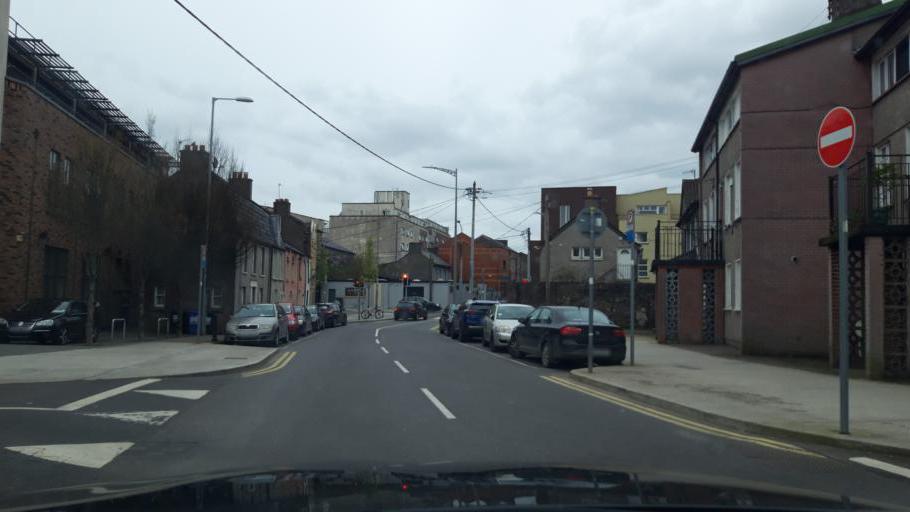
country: IE
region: Munster
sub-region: County Cork
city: Cork
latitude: 51.8996
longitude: -8.4814
